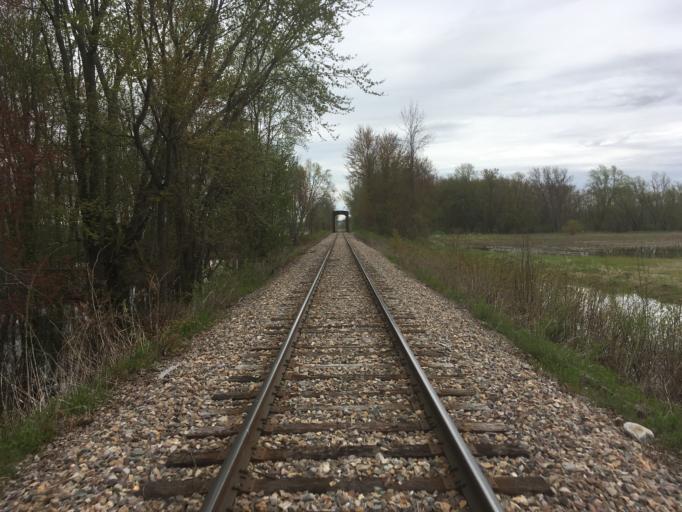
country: US
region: Vermont
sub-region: Addison County
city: Middlebury (village)
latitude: 43.9533
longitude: -73.1621
